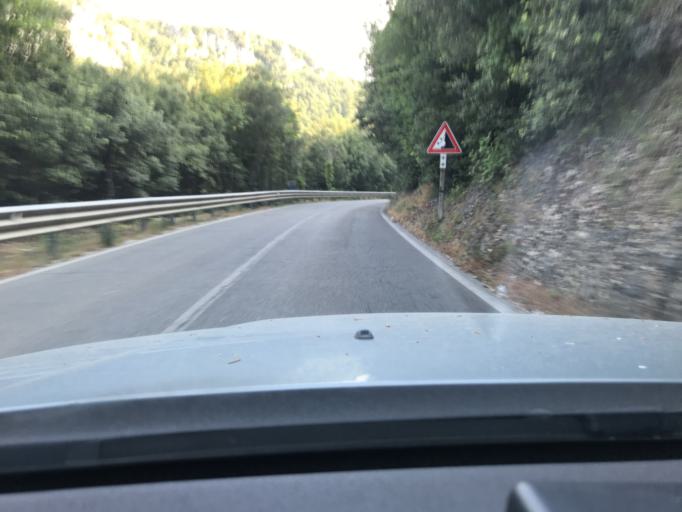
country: IT
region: Umbria
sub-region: Provincia di Terni
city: Amelia
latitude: 42.5579
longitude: 12.4091
